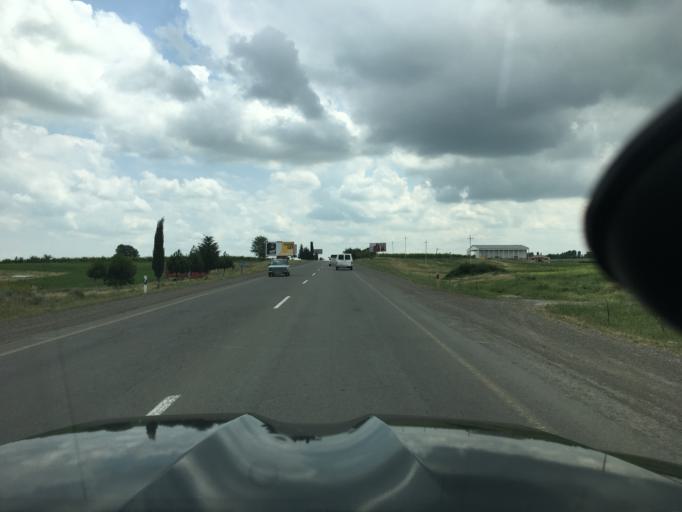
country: AZ
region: Tovuz
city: Tovuz
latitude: 40.9739
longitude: 45.6791
